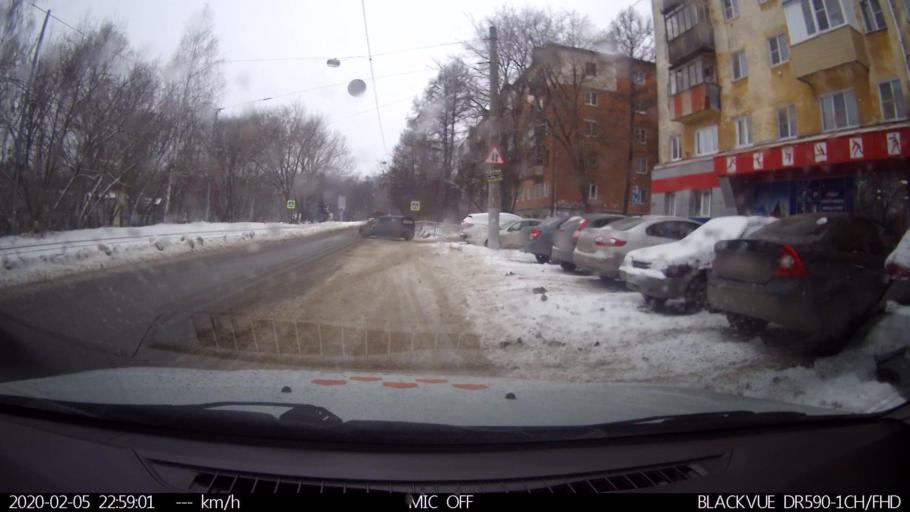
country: RU
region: Penza
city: Bogoslovka
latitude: 53.2170
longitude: 44.8603
